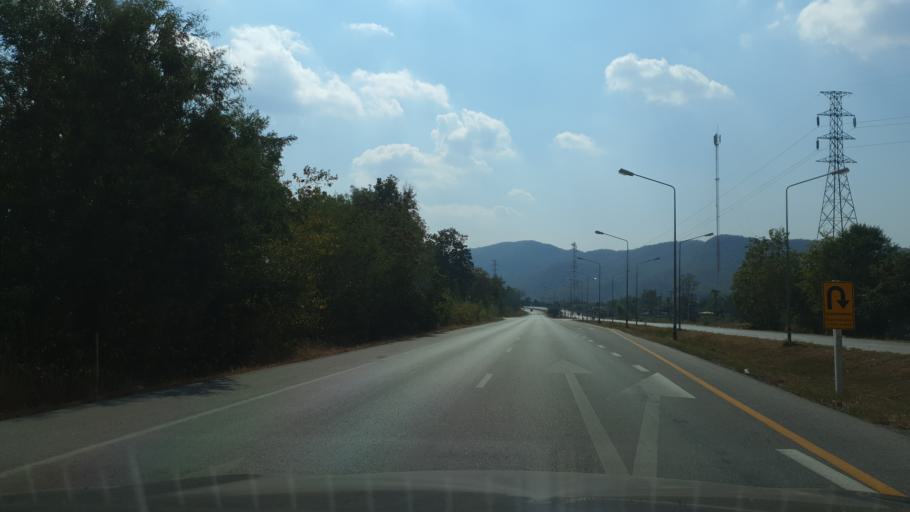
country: TH
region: Lampang
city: Mae Phrik
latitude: 17.3695
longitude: 99.1481
